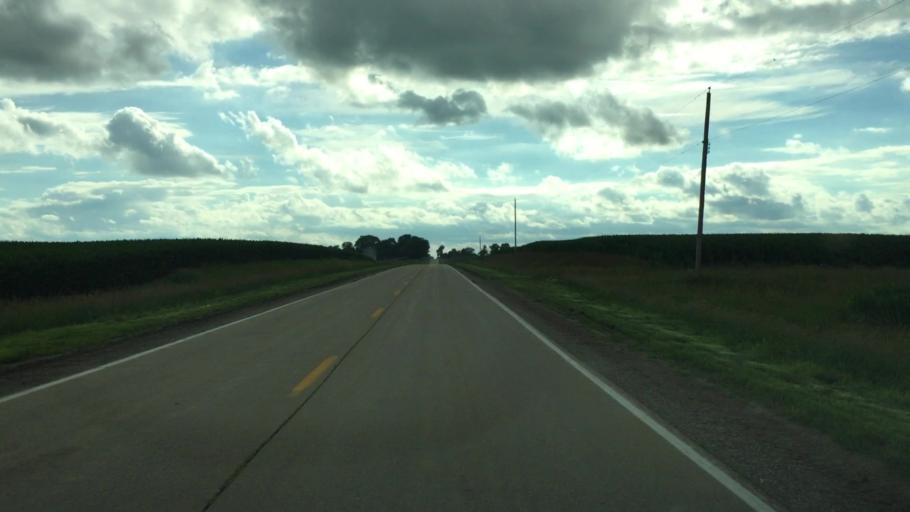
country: US
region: Iowa
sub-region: Jasper County
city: Monroe
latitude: 41.5807
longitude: -93.1305
